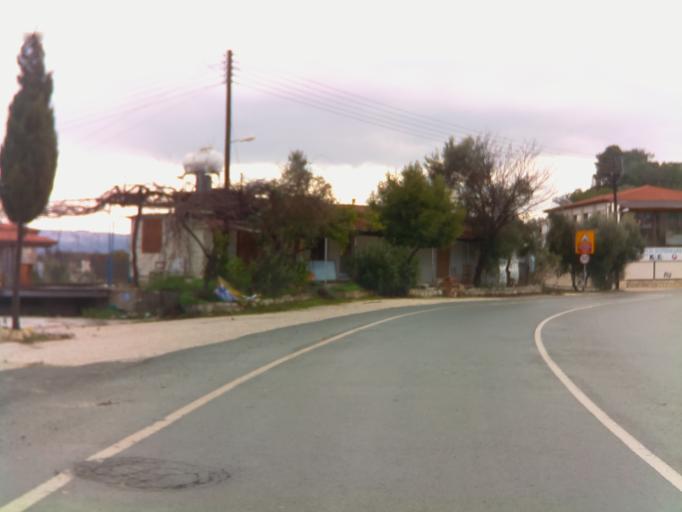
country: CY
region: Pafos
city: Tala
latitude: 34.8913
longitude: 32.4767
